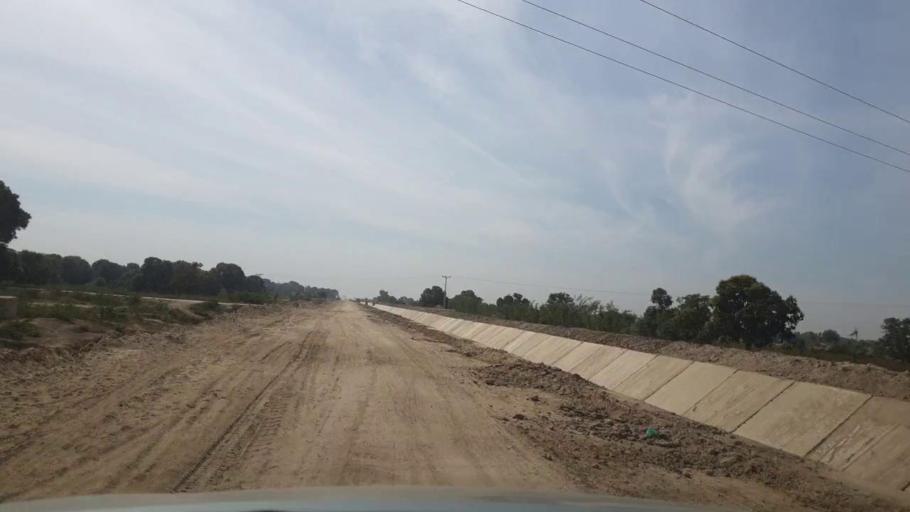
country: PK
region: Sindh
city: Kunri
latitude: 25.1477
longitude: 69.5883
